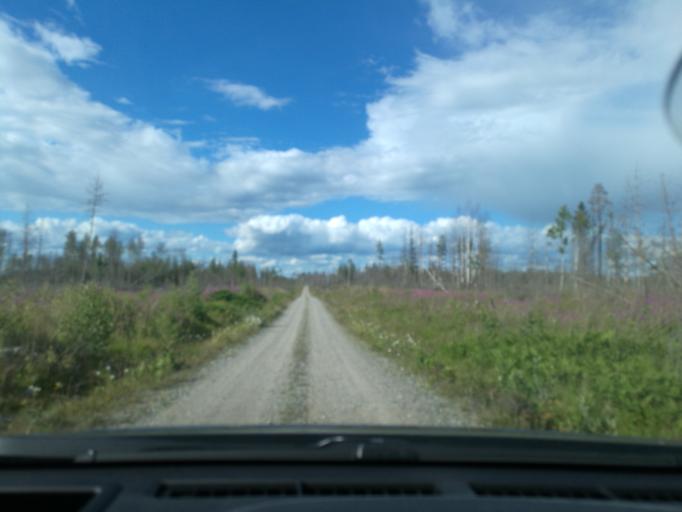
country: SE
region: Vaestmanland
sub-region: Surahammars Kommun
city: Ramnas
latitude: 59.8488
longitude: 16.2492
